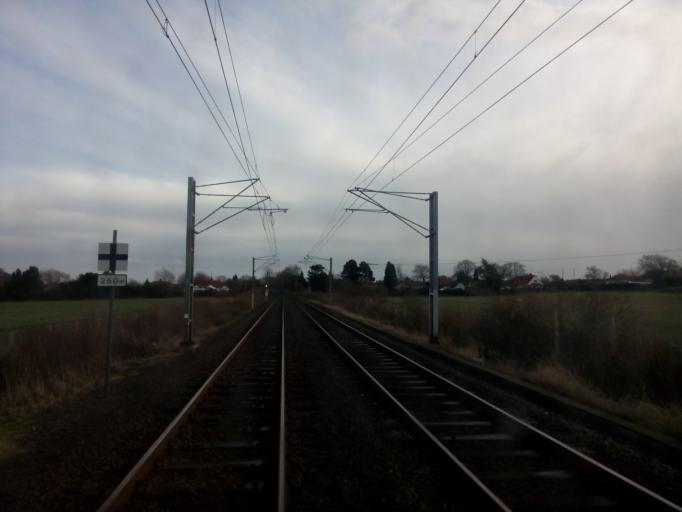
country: GB
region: England
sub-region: Newcastle upon Tyne
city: Dinnington
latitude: 55.0152
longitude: -1.6829
